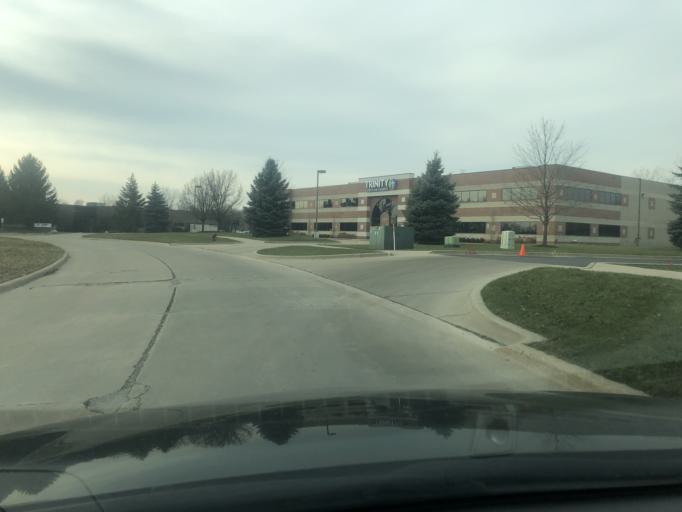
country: US
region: Michigan
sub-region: Wayne County
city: Southgate
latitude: 42.2101
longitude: -83.2304
